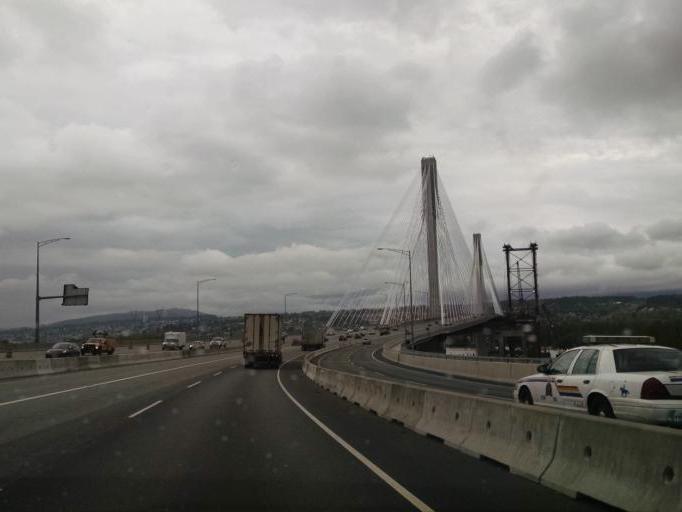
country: CA
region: British Columbia
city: Port Moody
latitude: 49.2116
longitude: -122.8088
